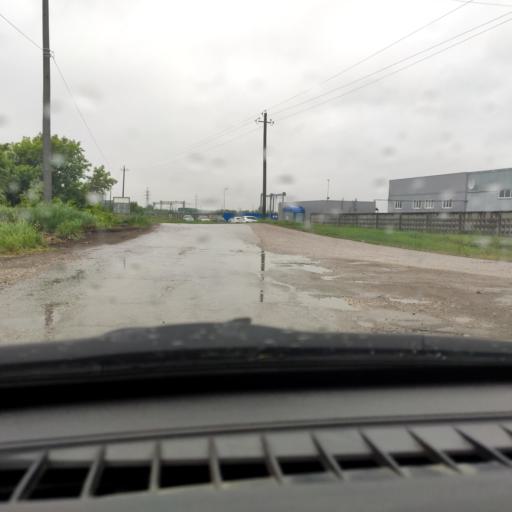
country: RU
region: Samara
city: Tol'yatti
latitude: 53.5686
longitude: 49.3615
